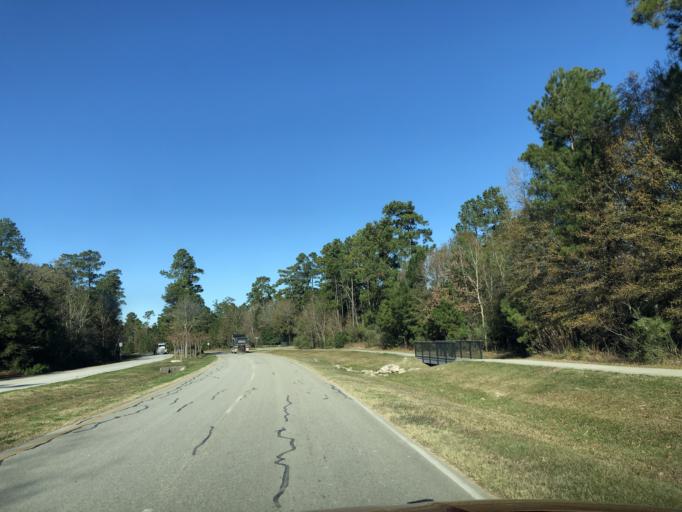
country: US
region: Texas
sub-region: Montgomery County
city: Porter Heights
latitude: 30.0862
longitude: -95.3348
